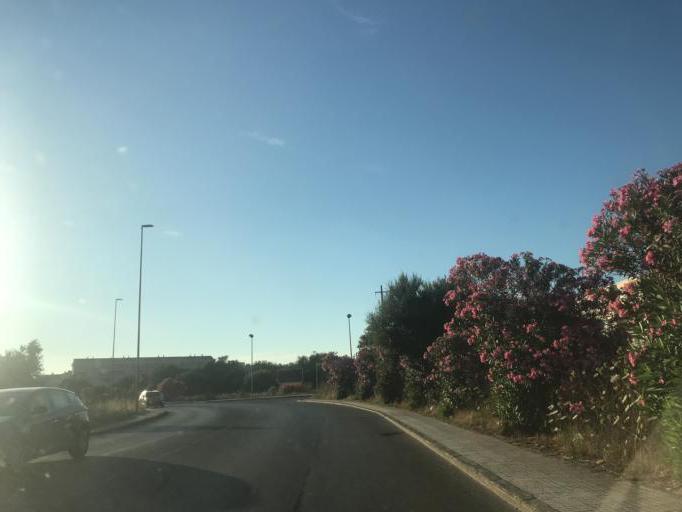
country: IT
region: Sardinia
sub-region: Provincia di Sassari
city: Alghero
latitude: 40.5691
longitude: 8.3288
